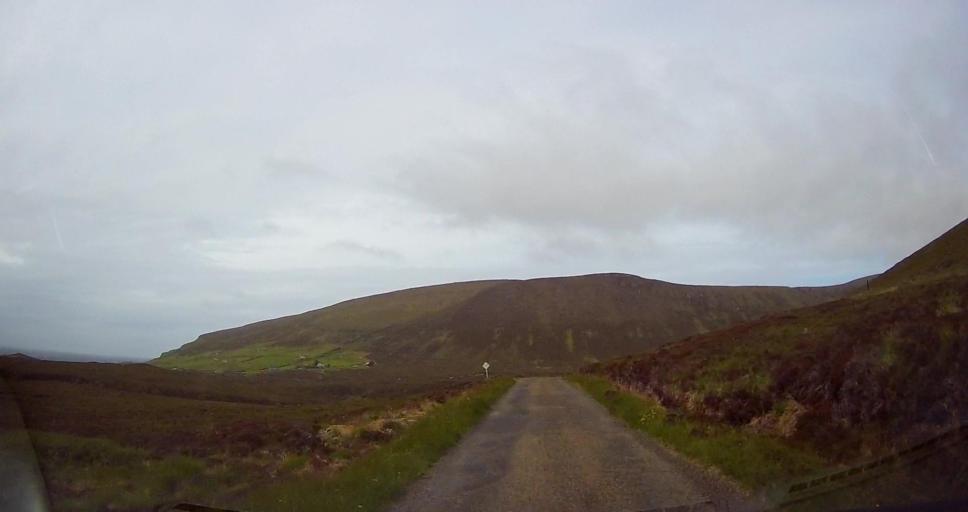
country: GB
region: Scotland
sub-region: Orkney Islands
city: Stromness
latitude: 58.8815
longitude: -3.3711
